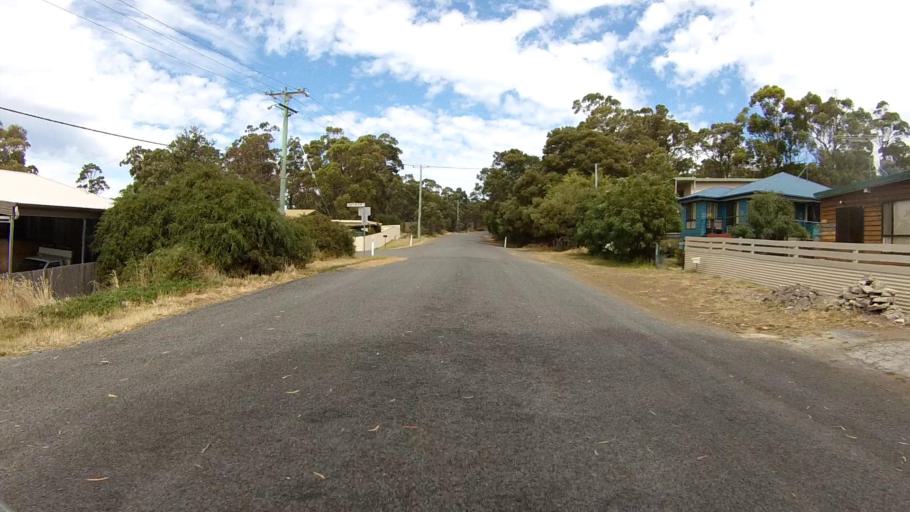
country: AU
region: Tasmania
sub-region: Sorell
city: Sorell
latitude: -42.8934
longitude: 147.6867
